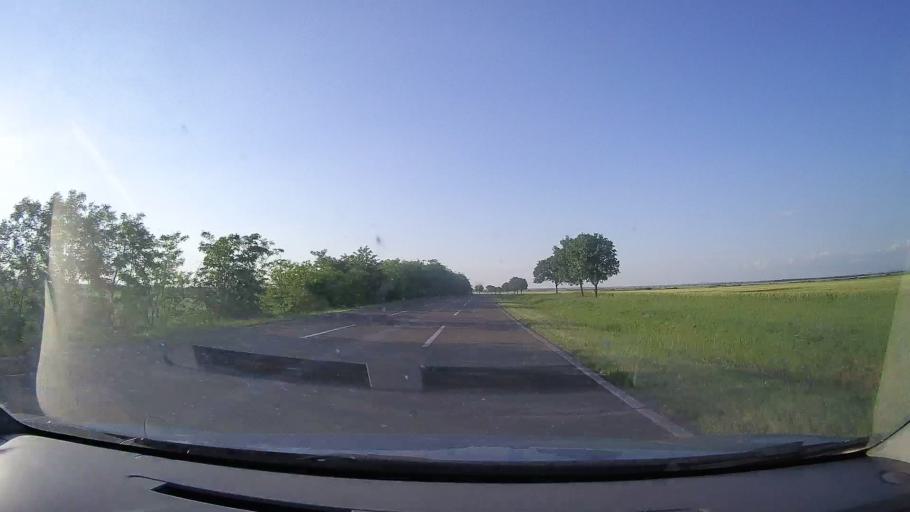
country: RO
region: Timis
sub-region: Comuna Moravita
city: Moravita
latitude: 45.2141
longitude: 21.2997
